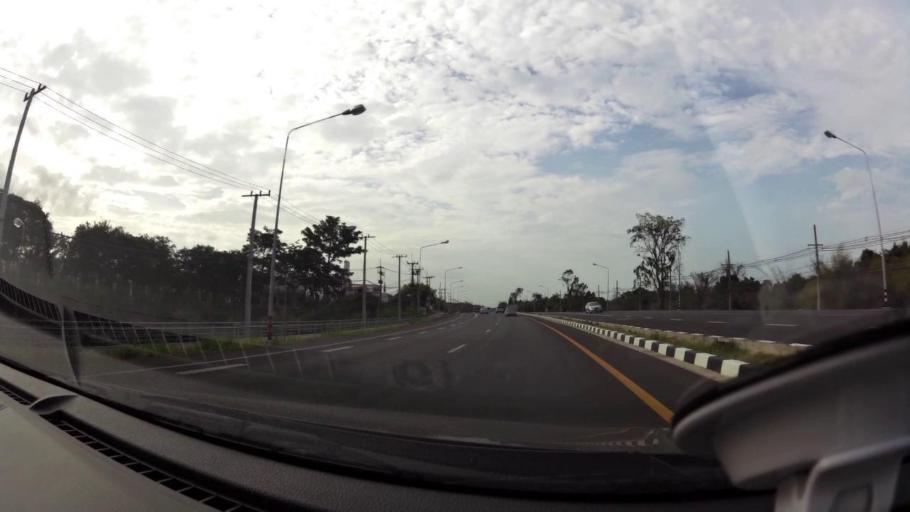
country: TH
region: Prachuap Khiri Khan
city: Hua Hin
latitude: 12.4787
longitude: 99.9719
